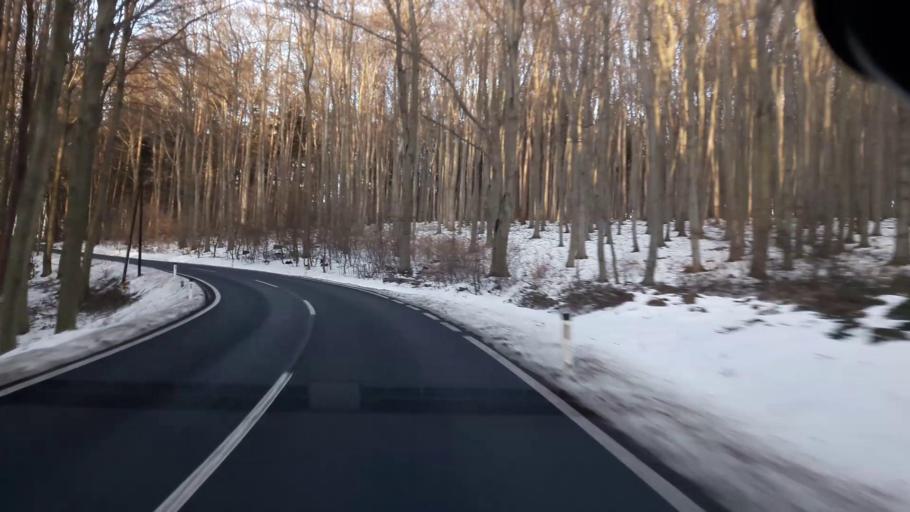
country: AT
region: Lower Austria
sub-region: Politischer Bezirk Wien-Umgebung
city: Mauerbach
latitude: 48.2766
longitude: 16.1704
